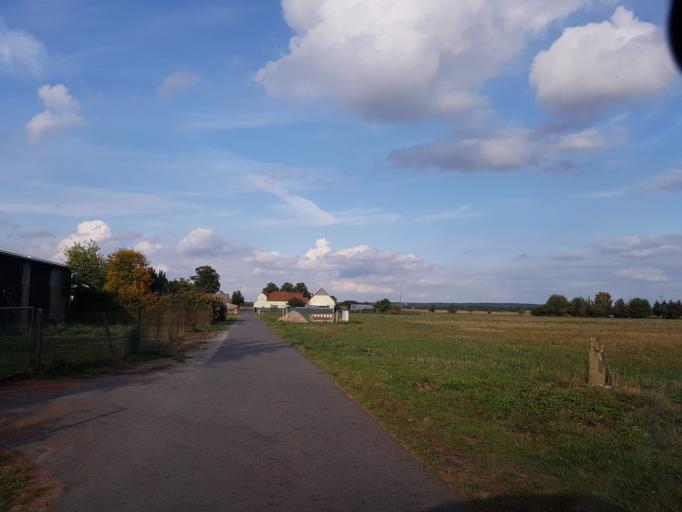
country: DE
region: Saxony
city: Nauwalde
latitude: 51.4594
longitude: 13.4305
